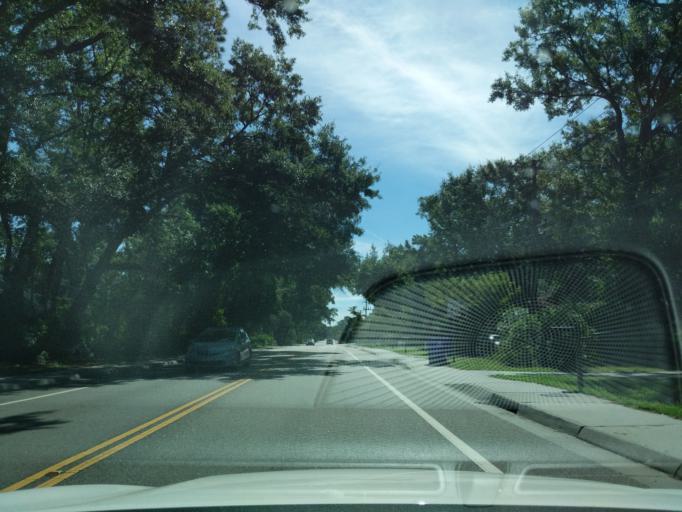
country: US
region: South Carolina
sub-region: Charleston County
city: Charleston
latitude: 32.7422
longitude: -79.9324
